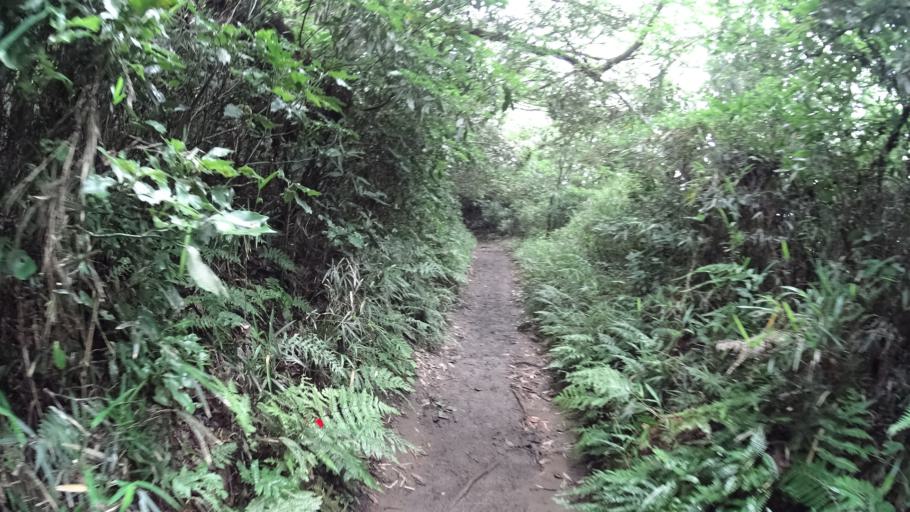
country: JP
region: Kanagawa
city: Zushi
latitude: 35.3387
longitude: 139.5880
